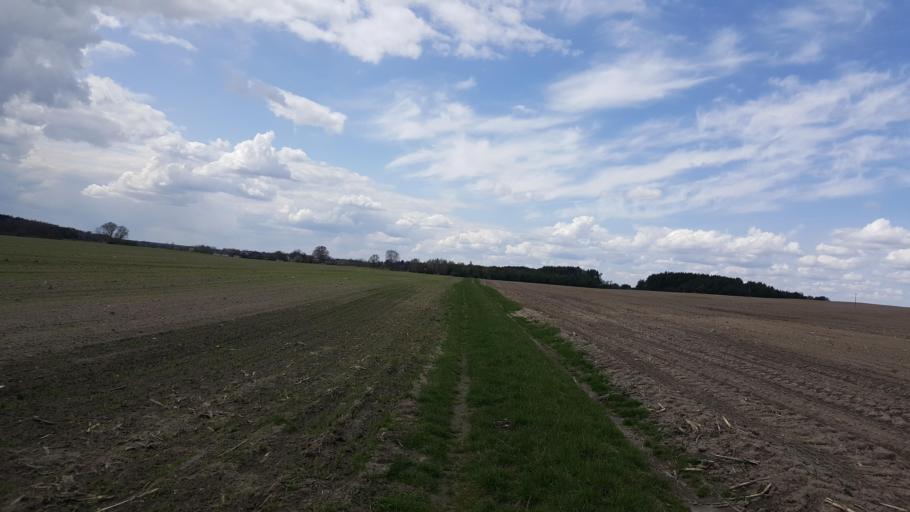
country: BY
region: Brest
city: Kamyanyets
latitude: 52.3516
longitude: 23.7188
